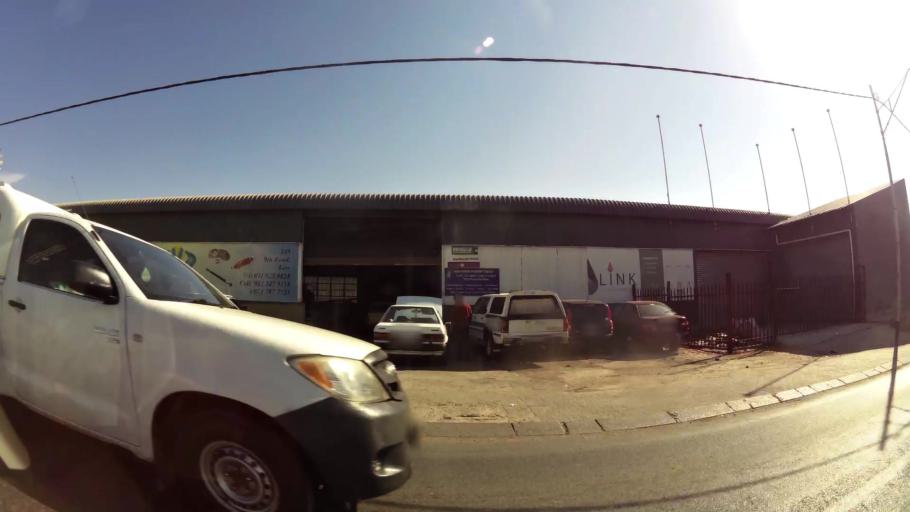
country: ZA
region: Gauteng
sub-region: City of Johannesburg Metropolitan Municipality
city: Modderfontein
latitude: -26.1164
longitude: 28.0999
